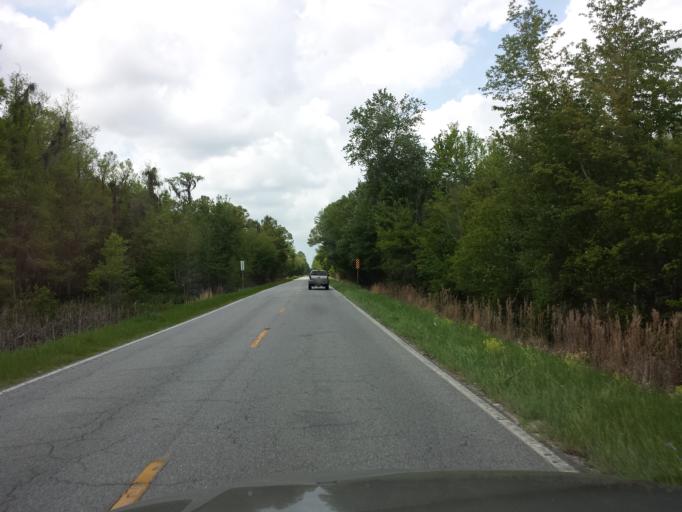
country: US
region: Georgia
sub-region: Echols County
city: Statenville
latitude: 30.6633
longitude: -83.1579
